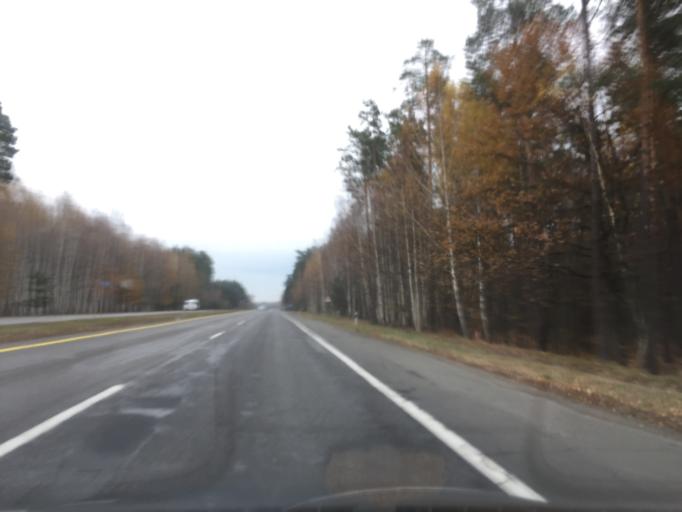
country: BY
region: Gomel
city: Horad Rechytsa
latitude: 52.3597
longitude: 30.6585
